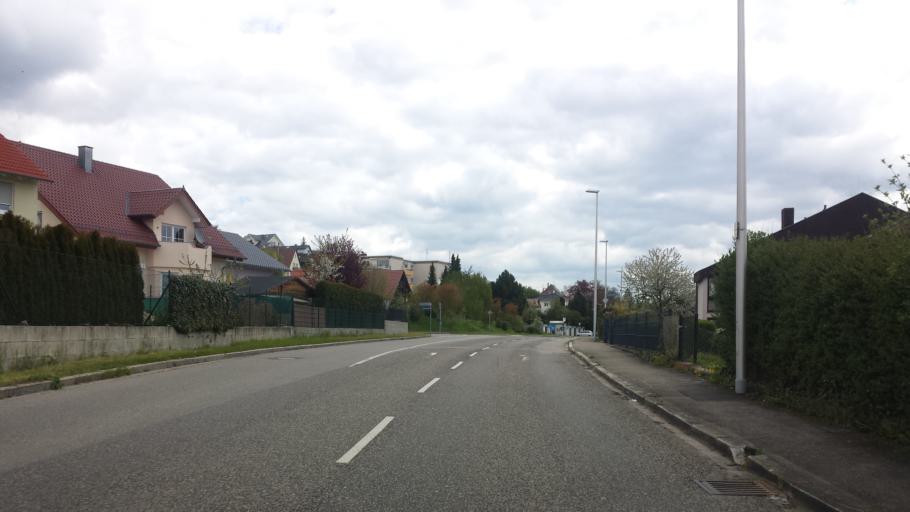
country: DE
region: Baden-Wuerttemberg
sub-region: Karlsruhe Region
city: Niefern-Oschelbronn
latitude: 48.9041
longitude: 8.8045
